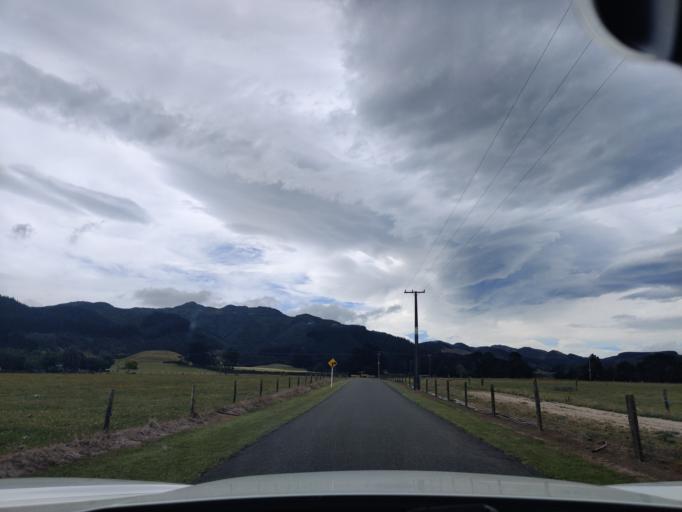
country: NZ
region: Wellington
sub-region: Masterton District
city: Masterton
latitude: -41.0313
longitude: 175.4462
